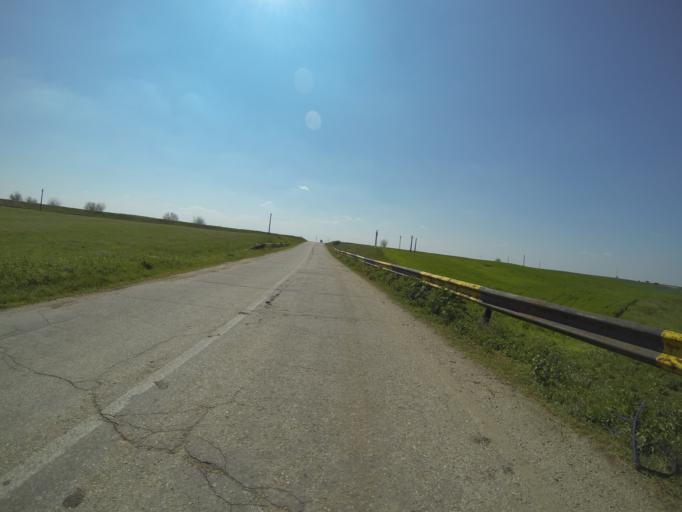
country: RO
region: Dolj
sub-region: Comuna Unirea
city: Unirea
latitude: 44.1756
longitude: 23.1961
